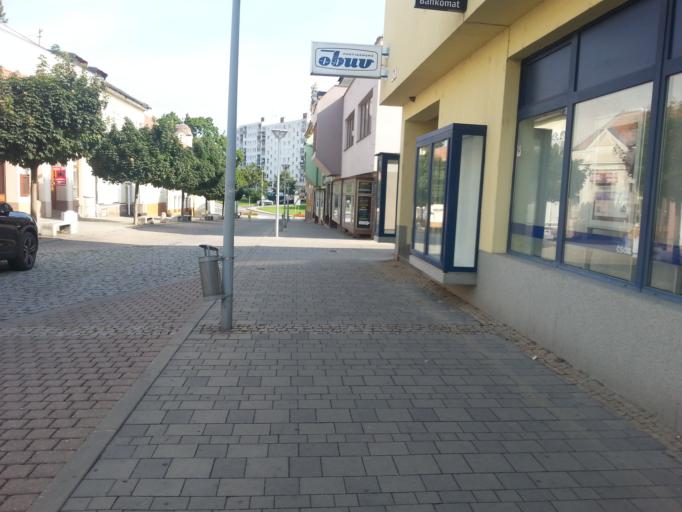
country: SK
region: Trenciansky
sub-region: Okres Nove Mesto nad Vahom
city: Nove Mesto nad Vahom
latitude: 48.7593
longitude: 17.8312
